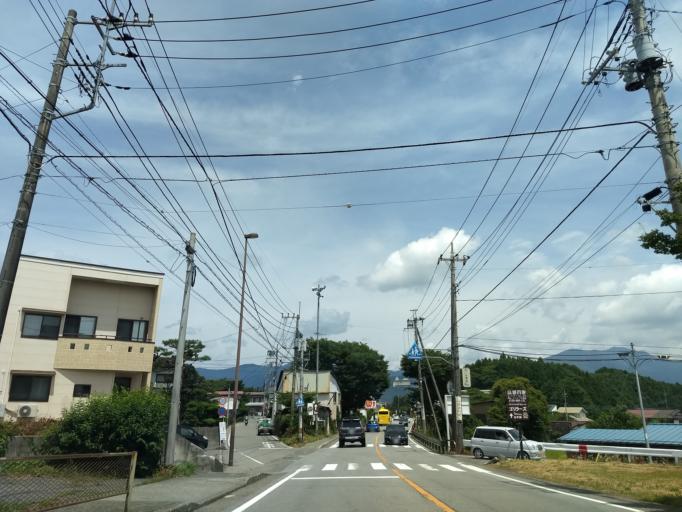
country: JP
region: Yamanashi
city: Fujikawaguchiko
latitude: 35.4654
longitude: 138.8024
